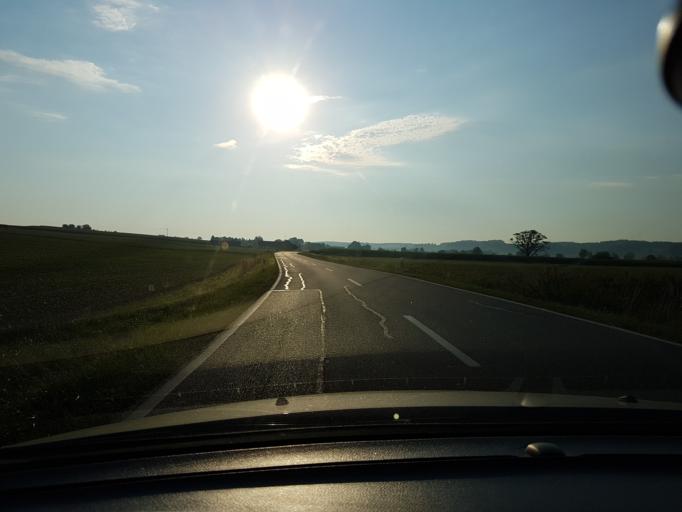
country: DE
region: Bavaria
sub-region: Lower Bavaria
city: Schalkham
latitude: 48.4979
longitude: 12.4007
